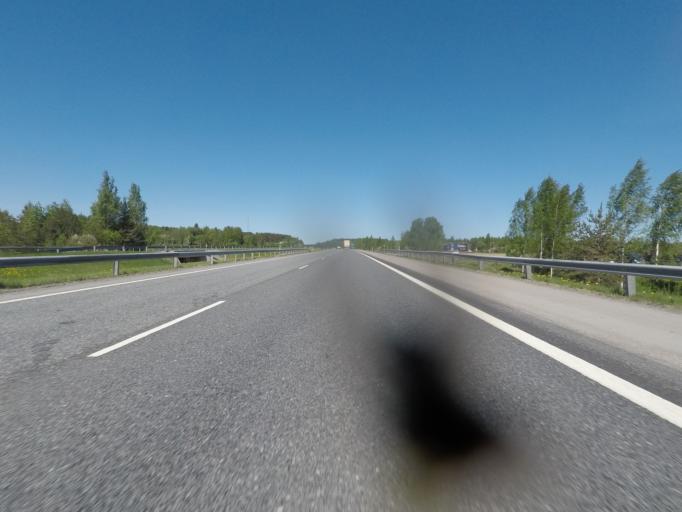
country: FI
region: Haeme
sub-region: Haemeenlinna
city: Janakkala
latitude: 60.9012
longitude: 24.5561
